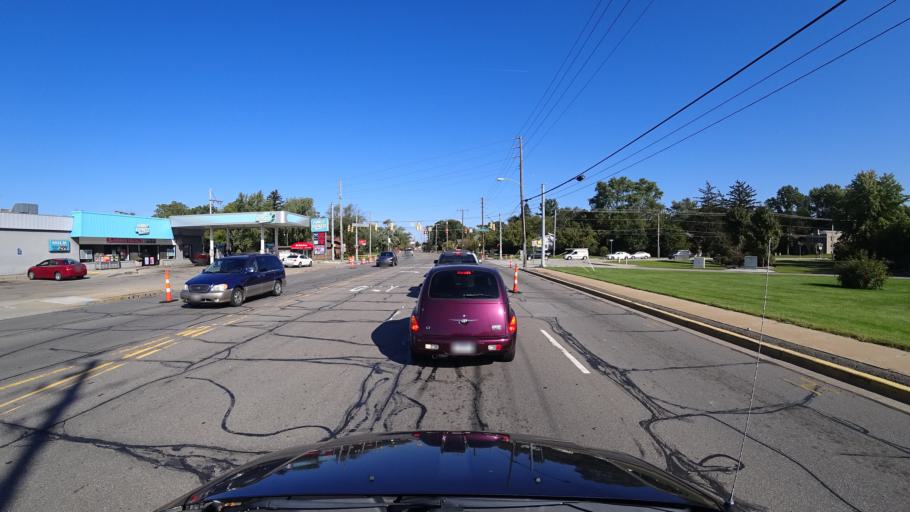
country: US
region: Indiana
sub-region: LaPorte County
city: Michigan City
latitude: 41.6942
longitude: -86.8937
